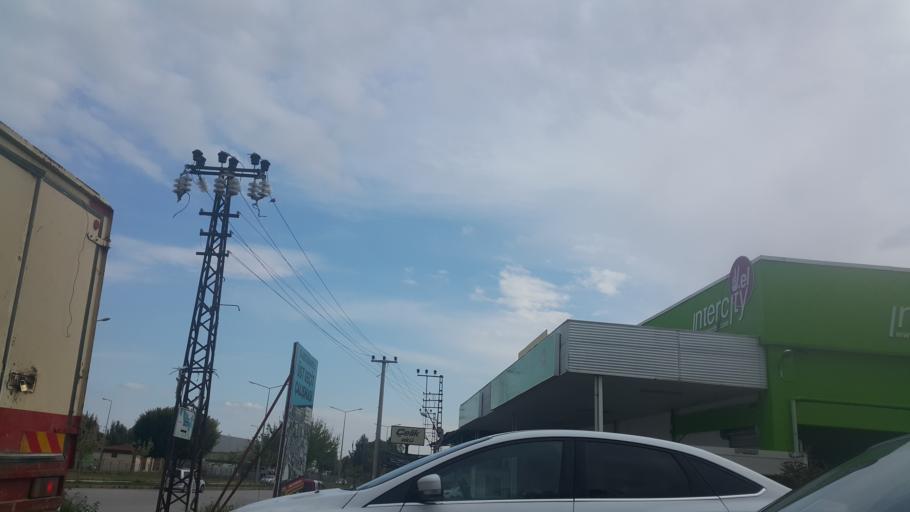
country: TR
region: Adana
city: Seyhan
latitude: 36.9972
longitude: 35.2448
